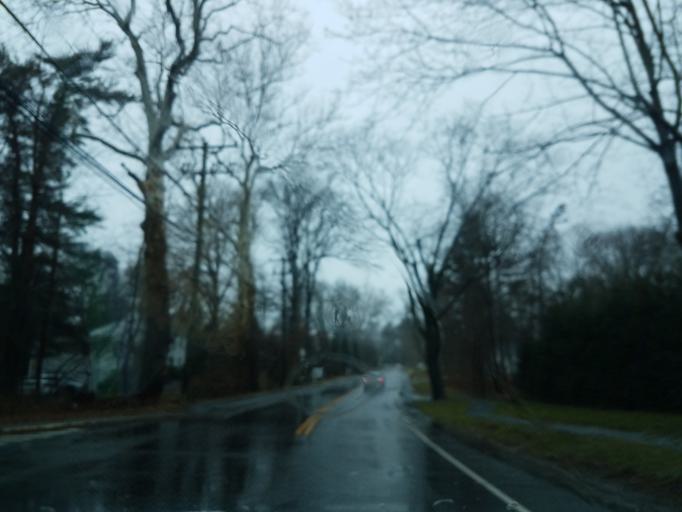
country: US
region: Connecticut
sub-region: Fairfield County
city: Westport
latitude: 41.1431
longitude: -73.3281
